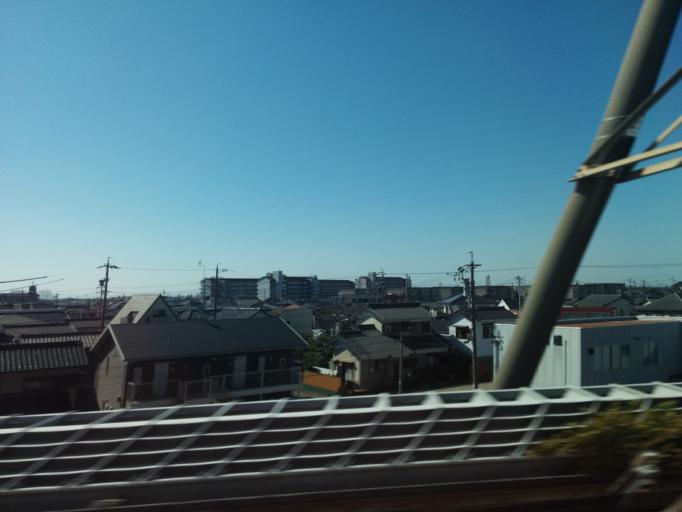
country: JP
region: Aichi
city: Anjo
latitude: 34.9358
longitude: 137.0911
